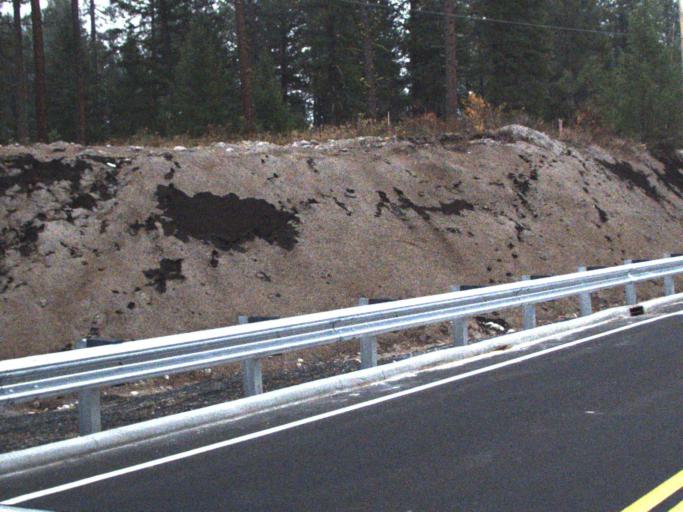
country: US
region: Washington
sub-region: Stevens County
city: Kettle Falls
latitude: 48.7365
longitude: -118.1328
